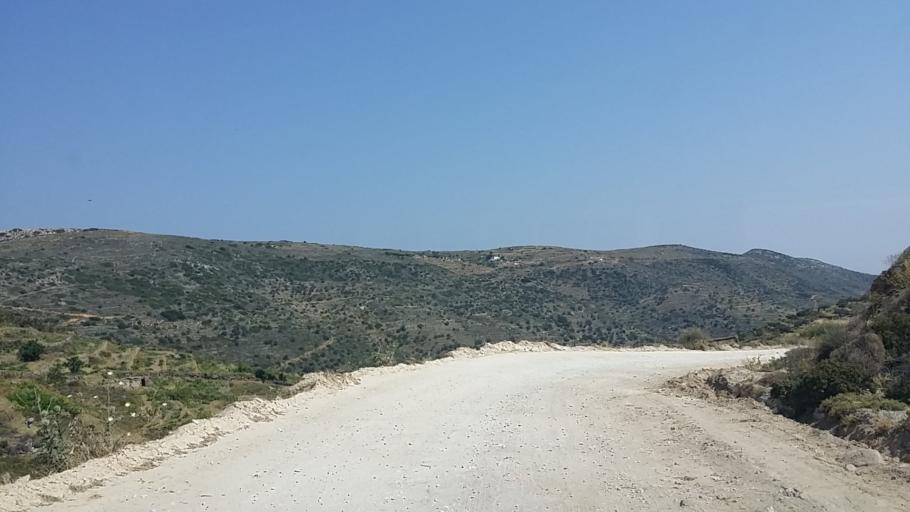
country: GR
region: South Aegean
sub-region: Nomos Kykladon
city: Paros
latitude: 37.0519
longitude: 25.2002
